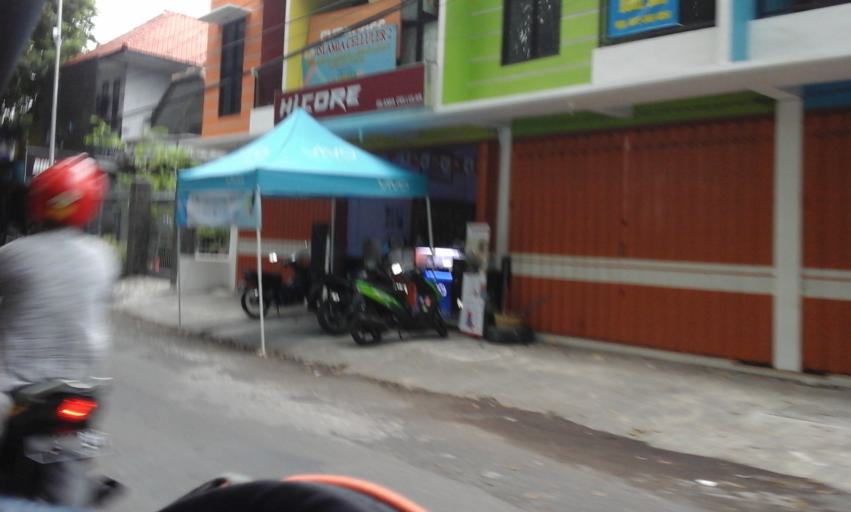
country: ID
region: East Java
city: Rogotrunan
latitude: -8.1184
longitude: 113.2266
